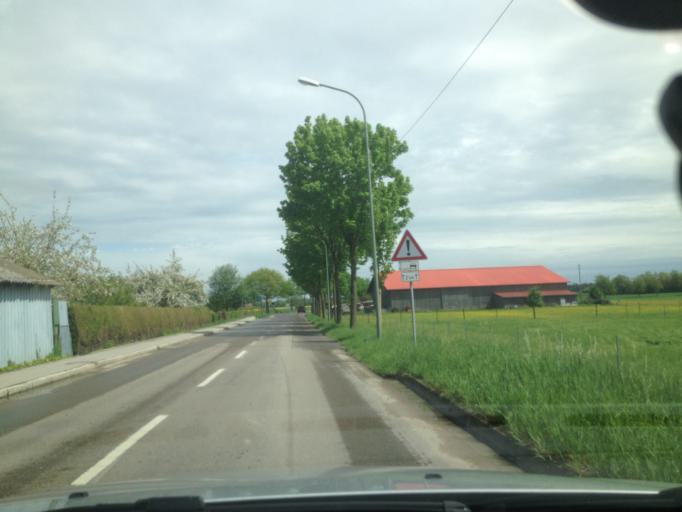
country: DE
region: Bavaria
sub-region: Swabia
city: Bobingen
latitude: 48.3144
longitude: 10.8205
